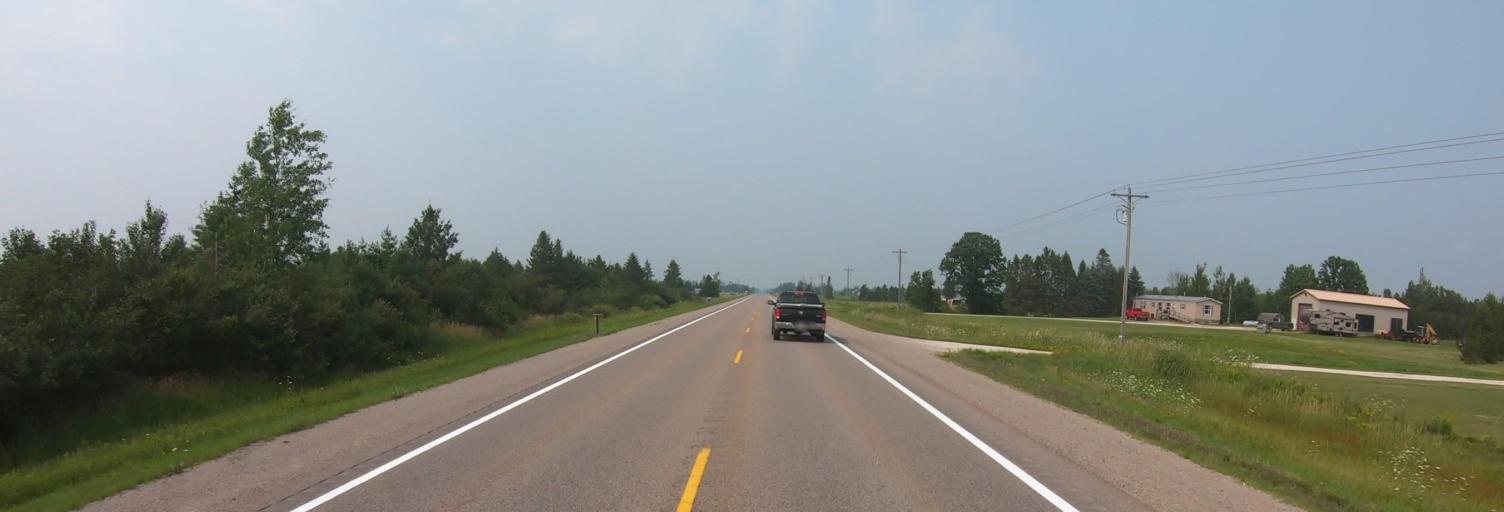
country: US
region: Michigan
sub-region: Chippewa County
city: Sault Ste. Marie
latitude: 46.3215
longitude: -84.3638
